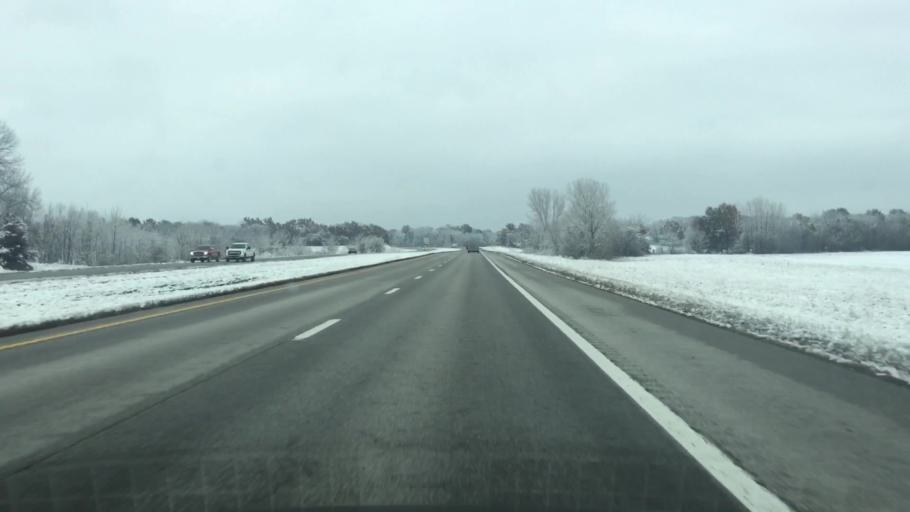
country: US
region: Missouri
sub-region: Cass County
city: Garden City
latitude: 38.5109
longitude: -94.1009
